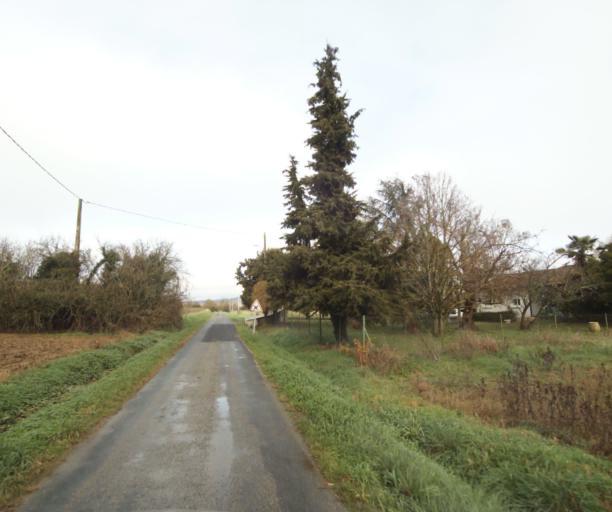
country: FR
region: Midi-Pyrenees
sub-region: Departement de la Haute-Garonne
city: Villemur-sur-Tarn
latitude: 43.8727
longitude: 1.4806
